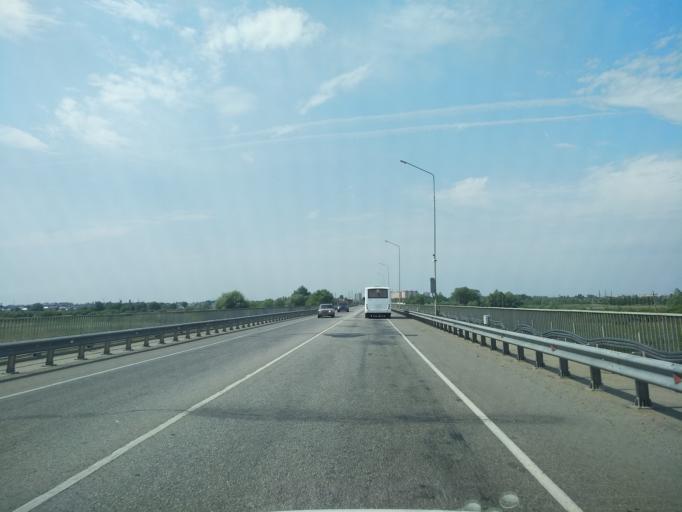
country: RU
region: Voronezj
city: Somovo
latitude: 51.6843
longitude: 39.3496
